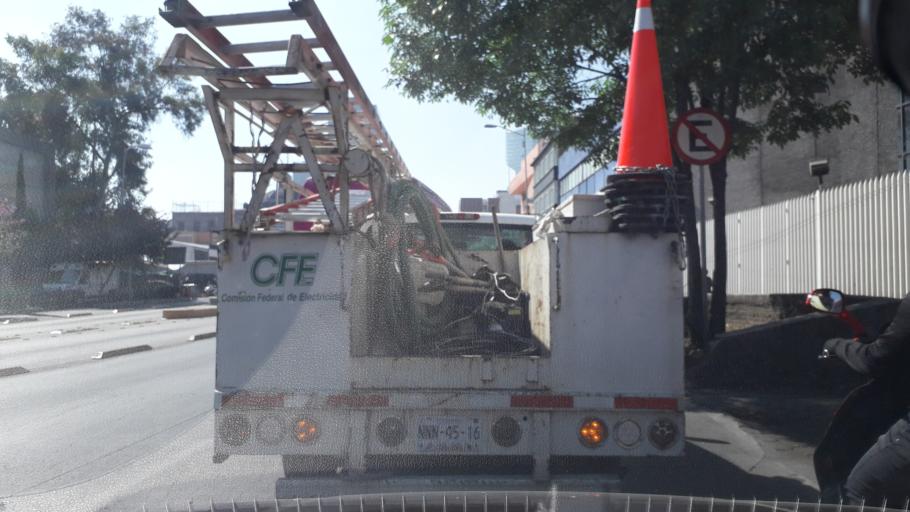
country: MX
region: Mexico City
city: Cuauhtemoc
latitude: 19.4416
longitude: -99.1483
